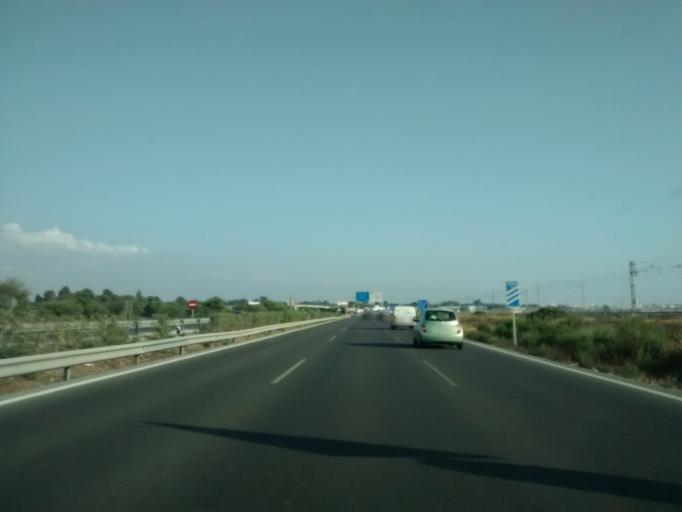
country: ES
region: Andalusia
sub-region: Provincia de Cadiz
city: Chiclana de la Frontera
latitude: 36.4483
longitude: -6.1490
